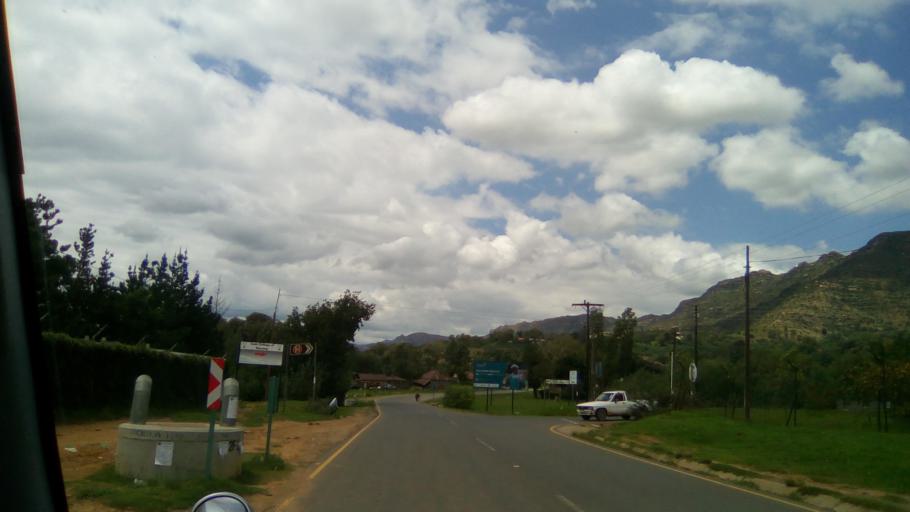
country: LS
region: Maseru
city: Nako
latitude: -29.6233
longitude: 27.5028
